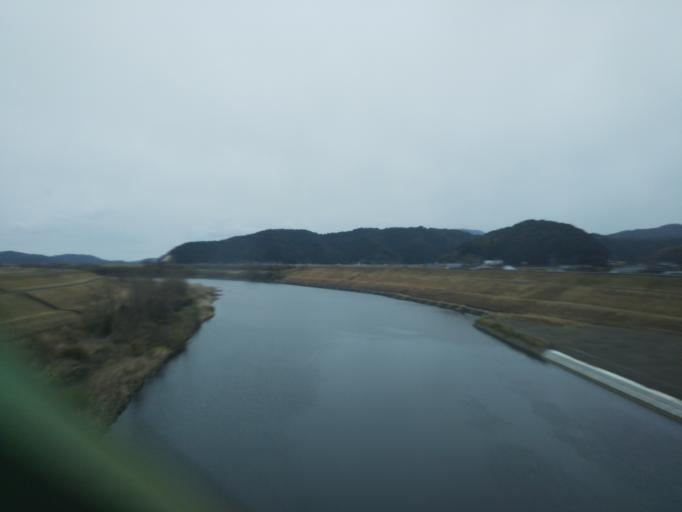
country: JP
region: Kochi
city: Nakamura
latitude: 32.9803
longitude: 132.9517
